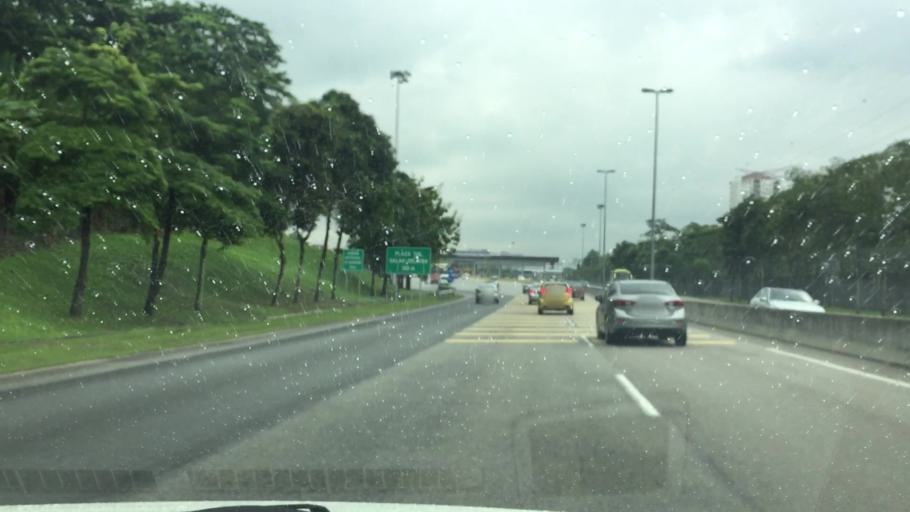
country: MY
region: Kuala Lumpur
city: Kuala Lumpur
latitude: 3.1075
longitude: 101.7098
